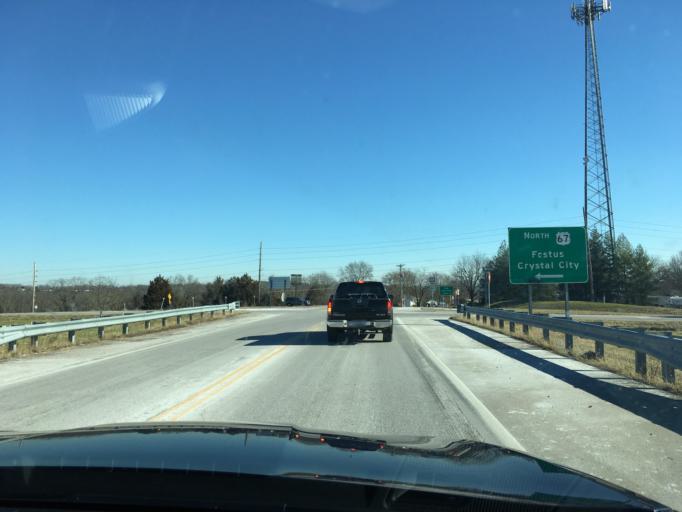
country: US
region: Missouri
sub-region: Jefferson County
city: De Soto
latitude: 38.1359
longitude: -90.4712
